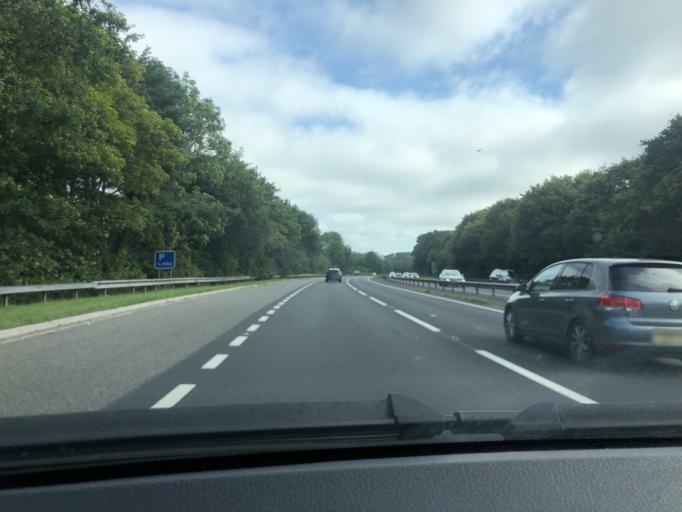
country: GB
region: England
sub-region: Devon
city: Honiton
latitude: 50.7961
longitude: -3.2080
